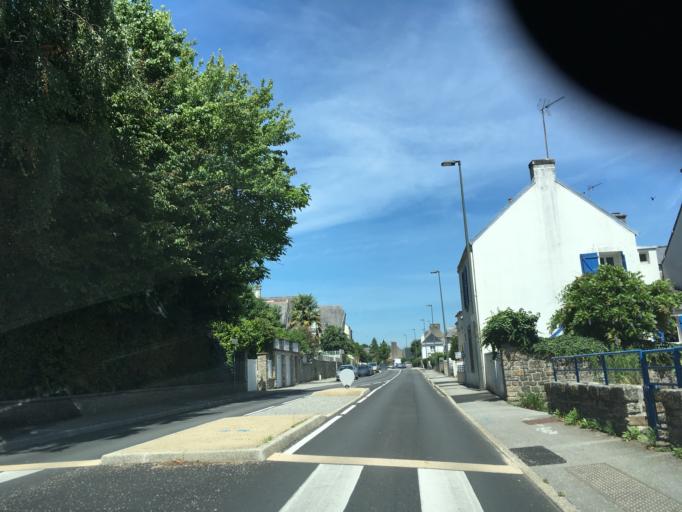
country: FR
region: Brittany
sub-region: Departement du Finistere
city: Quimper
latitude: 48.0057
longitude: -4.1183
